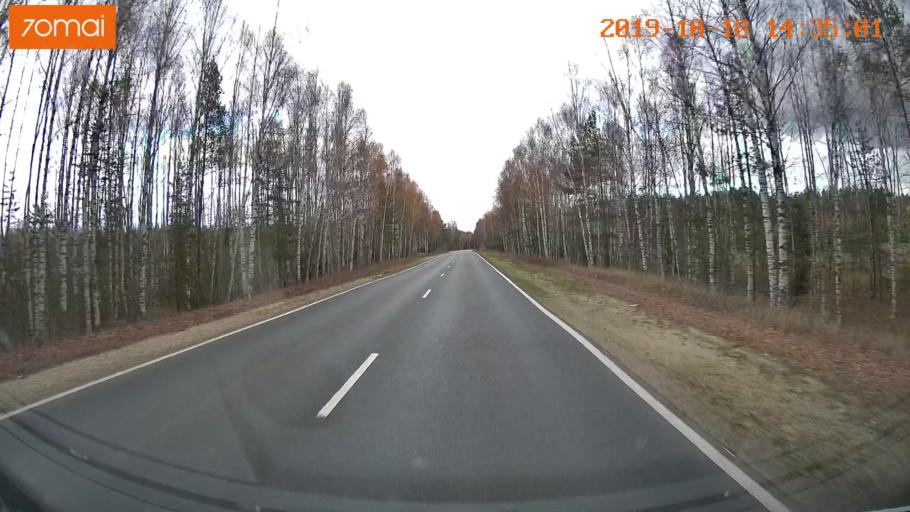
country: RU
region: Vladimir
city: Velikodvorskiy
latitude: 55.2186
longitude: 40.6279
